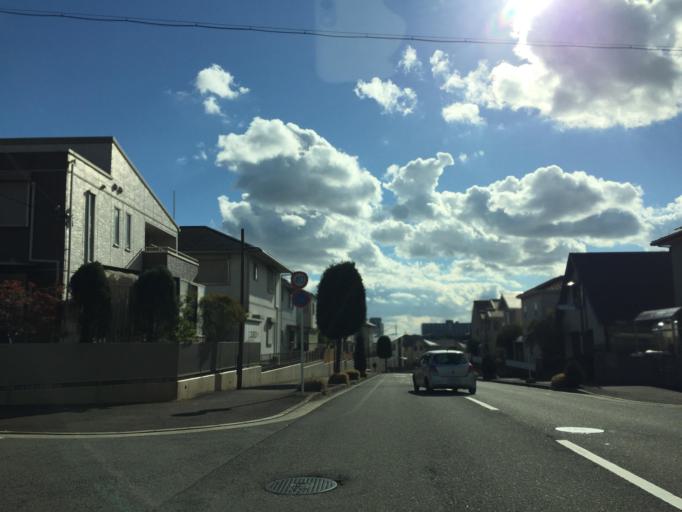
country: JP
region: Wakayama
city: Wakayama-shi
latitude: 34.2723
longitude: 135.1486
